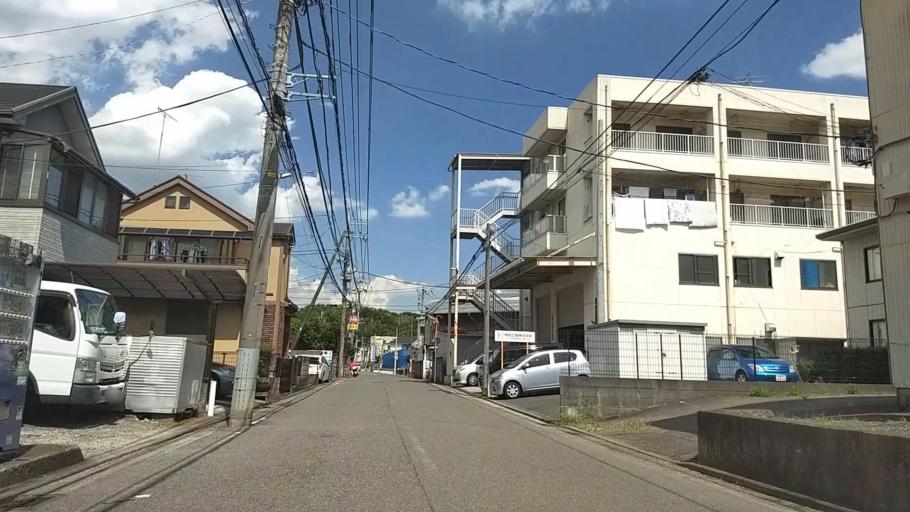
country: JP
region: Kanagawa
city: Yokohama
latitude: 35.5210
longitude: 139.5843
